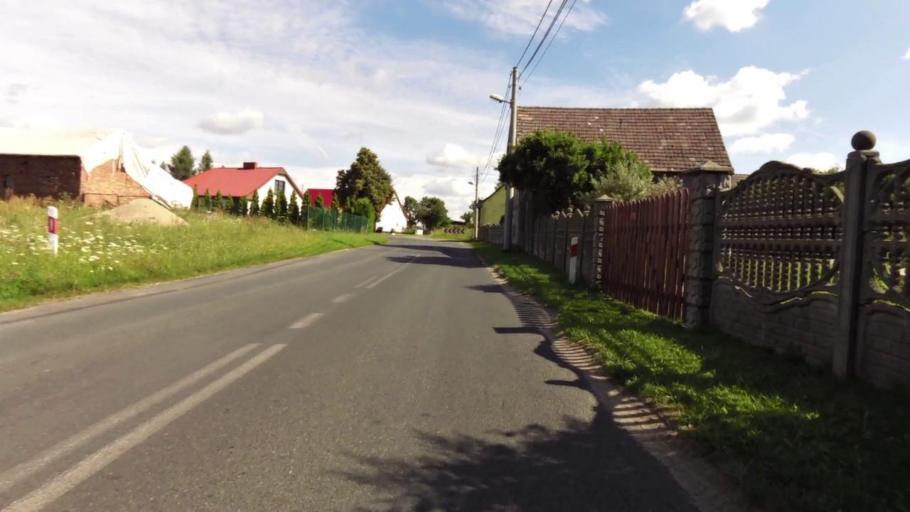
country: PL
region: West Pomeranian Voivodeship
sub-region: Powiat stargardzki
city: Dobrzany
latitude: 53.4042
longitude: 15.4326
